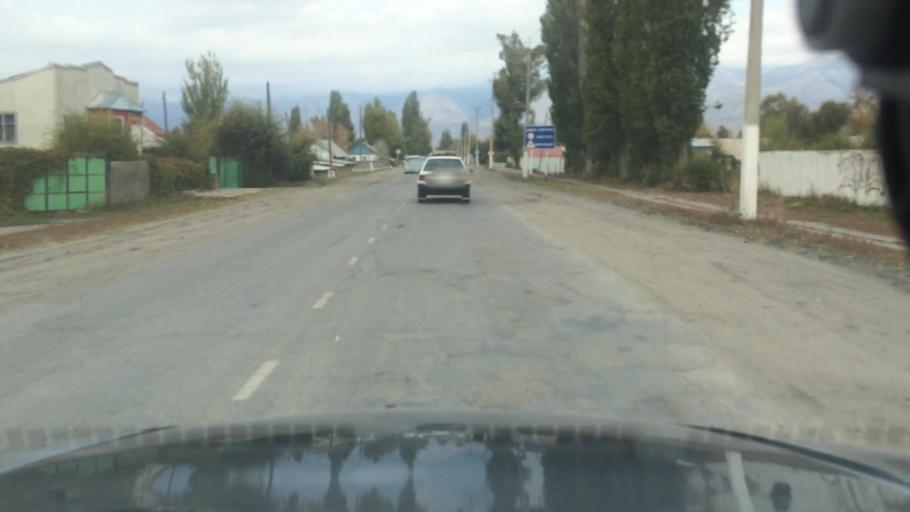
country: KG
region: Ysyk-Koel
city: Tyup
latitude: 42.7230
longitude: 78.3666
